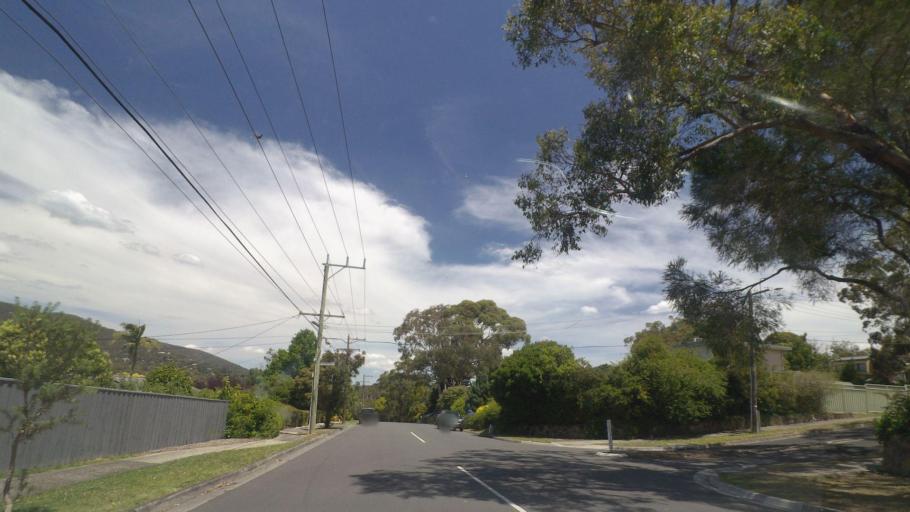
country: AU
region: Victoria
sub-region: Maroondah
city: Bayswater North
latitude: -37.8466
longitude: 145.2922
